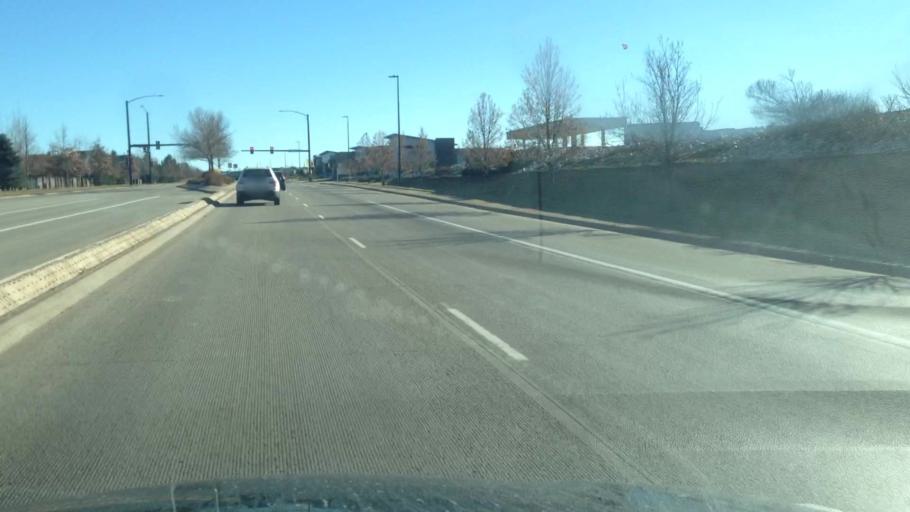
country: US
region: Colorado
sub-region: Arapahoe County
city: Dove Valley
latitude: 39.5755
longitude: -104.8069
